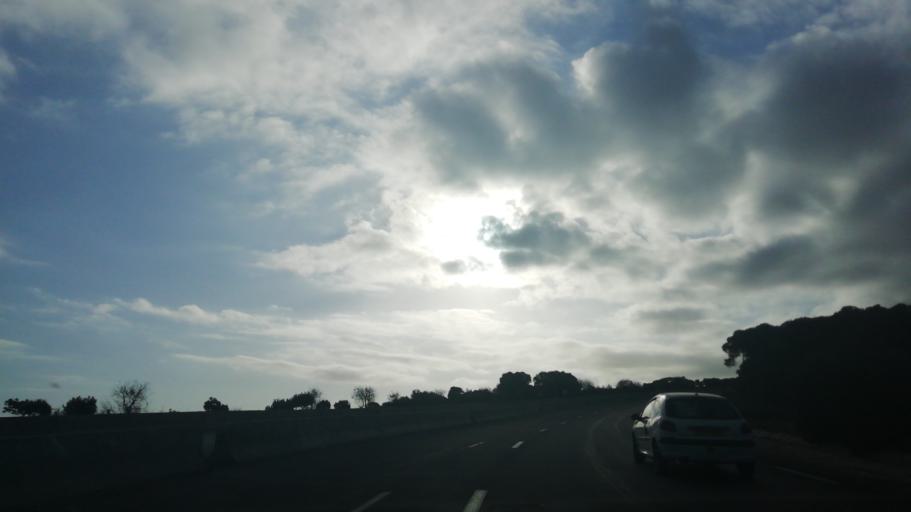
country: DZ
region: Mostaganem
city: Mostaganem
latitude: 36.1097
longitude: 0.2628
